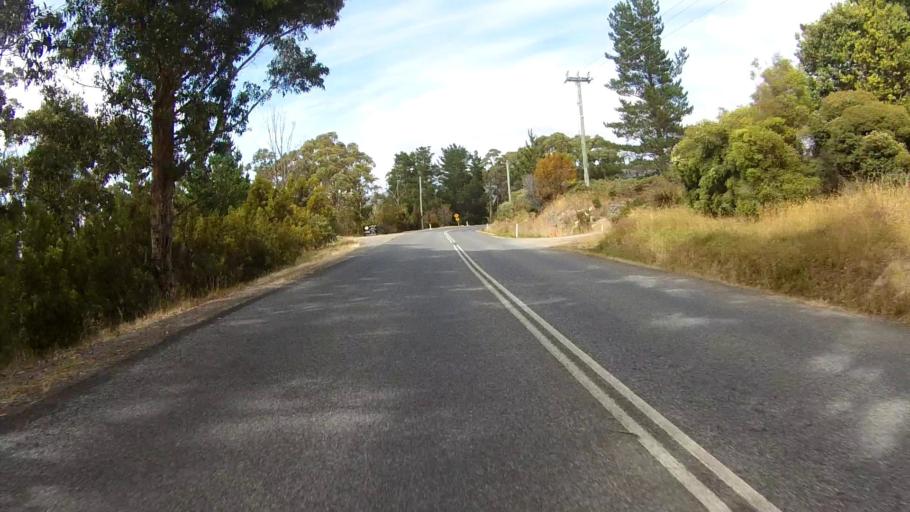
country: AU
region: Tasmania
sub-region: Kingborough
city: Kettering
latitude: -43.1451
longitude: 147.2429
